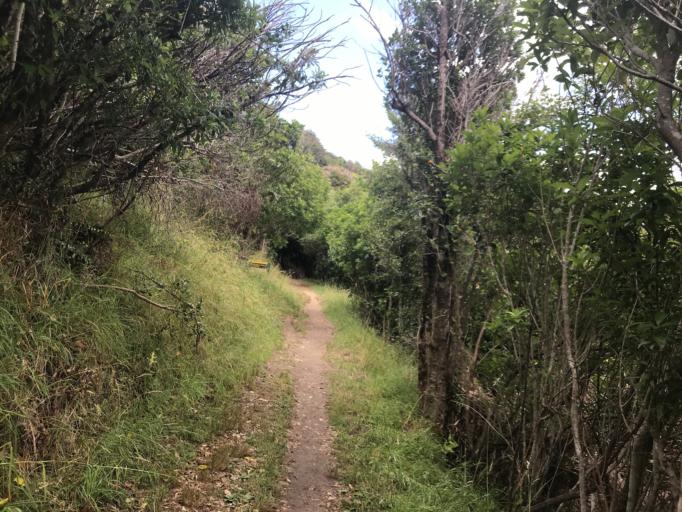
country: NZ
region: Marlborough
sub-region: Marlborough District
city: Picton
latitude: -41.2151
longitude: 173.9797
